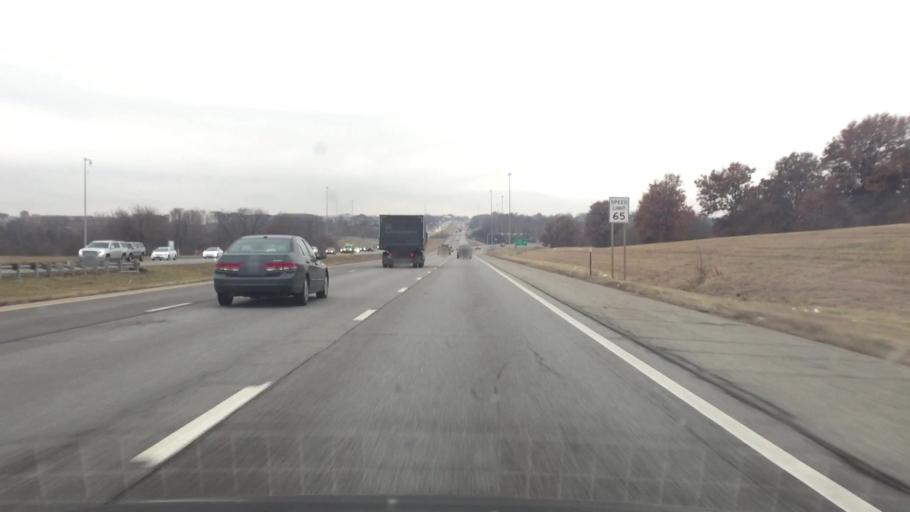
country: US
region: Kansas
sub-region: Johnson County
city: Lenexa
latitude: 38.8908
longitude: -94.6767
